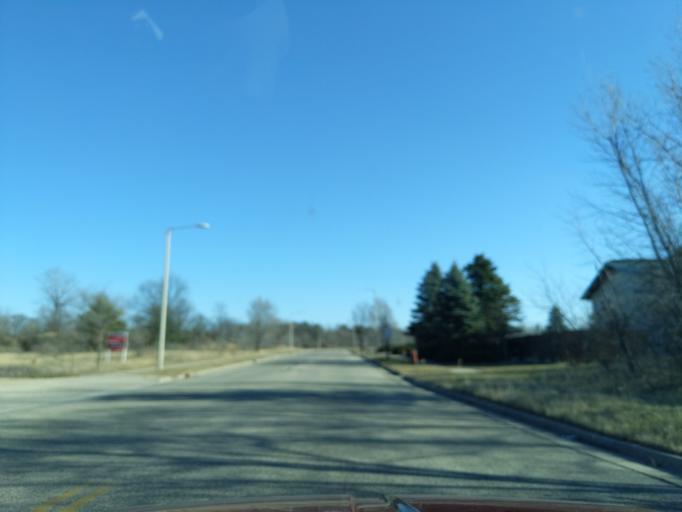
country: US
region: Wisconsin
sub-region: Waushara County
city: Wautoma
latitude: 44.0714
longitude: -89.2700
